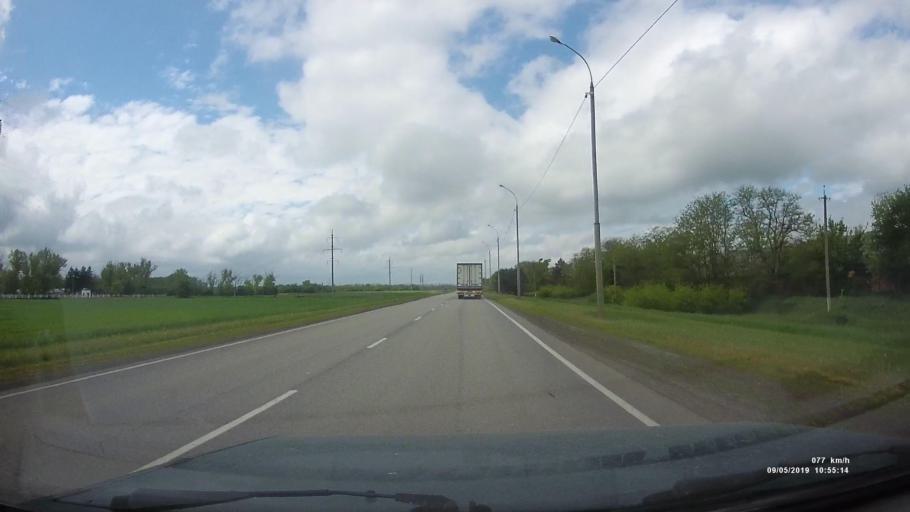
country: RU
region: Rostov
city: Peshkovo
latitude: 46.8739
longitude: 39.3185
